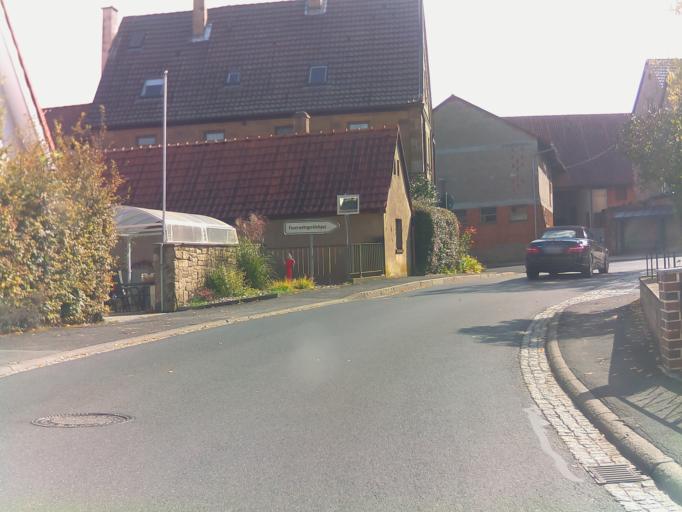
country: DE
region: Bavaria
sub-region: Regierungsbezirk Unterfranken
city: Biebelried
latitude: 49.7303
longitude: 10.0883
